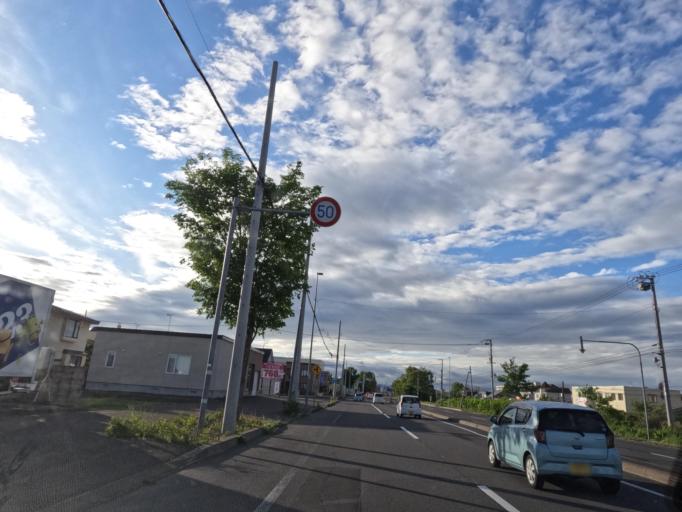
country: JP
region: Hokkaido
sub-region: Asahikawa-shi
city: Asahikawa
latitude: 43.7414
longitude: 142.3593
